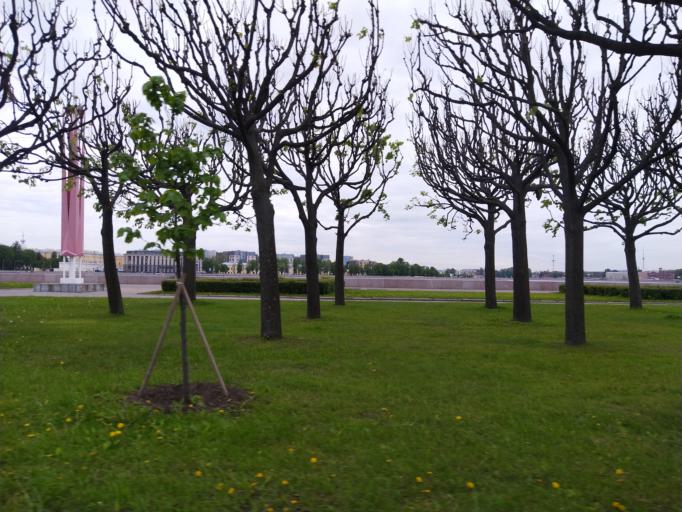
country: RU
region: Leningrad
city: Finlyandskiy
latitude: 59.9537
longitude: 30.4072
